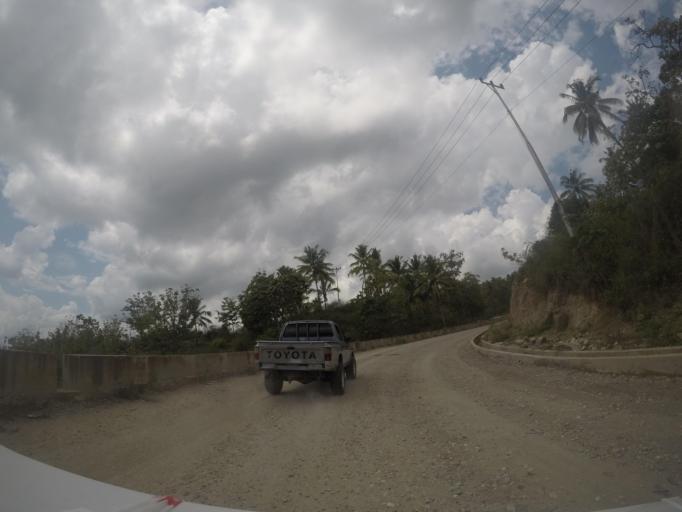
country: TL
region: Baucau
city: Baucau
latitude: -8.5330
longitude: 126.4258
